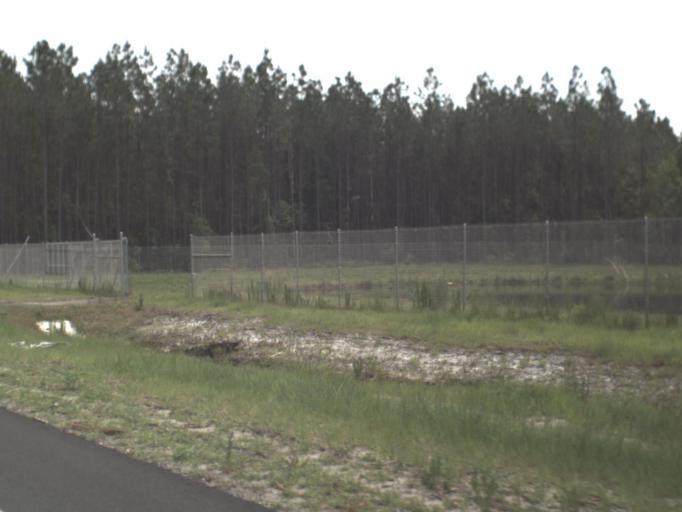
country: US
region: Florida
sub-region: Nassau County
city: Nassau Village-Ratliff
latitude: 30.4391
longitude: -81.9199
